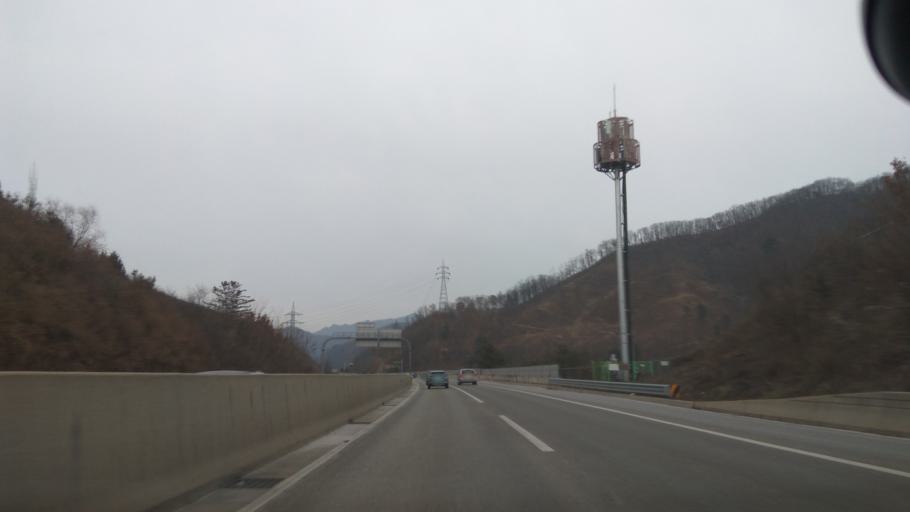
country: KR
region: Gyeonggi-do
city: Hwado
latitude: 37.6347
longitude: 127.3970
